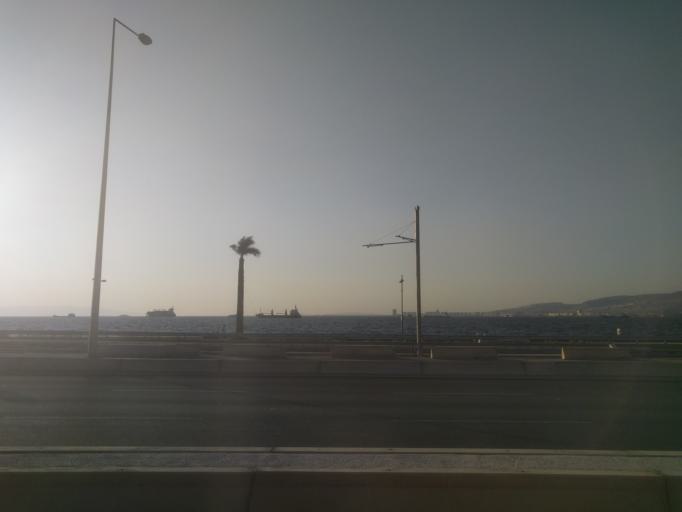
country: TR
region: Izmir
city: Izmir
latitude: 38.4147
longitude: 27.1226
